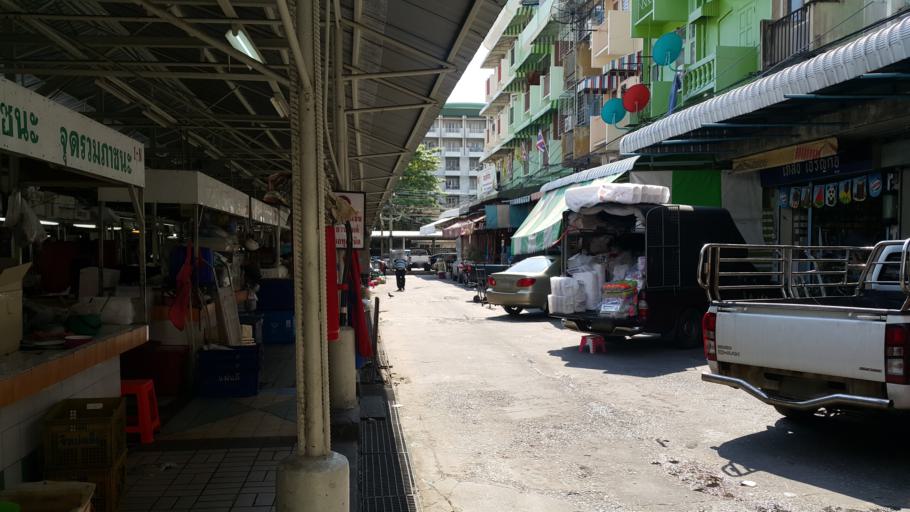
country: TH
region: Bangkok
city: Phra Khanong
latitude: 13.7106
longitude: 100.6010
